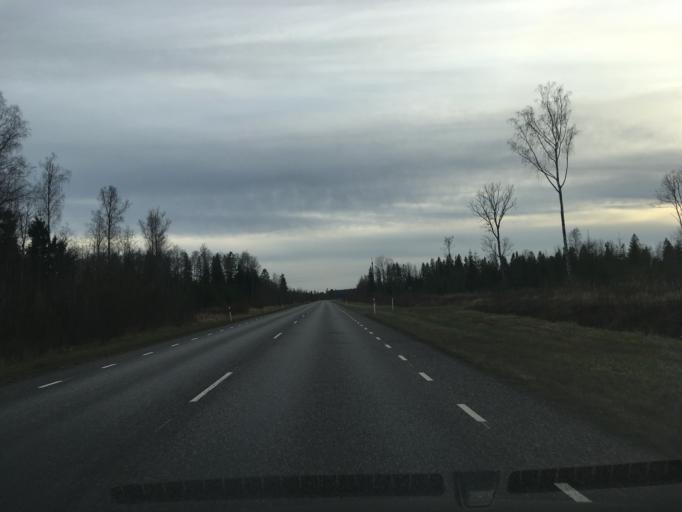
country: EE
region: Ida-Virumaa
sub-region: Johvi vald
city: Johvi
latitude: 59.3450
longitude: 27.4678
